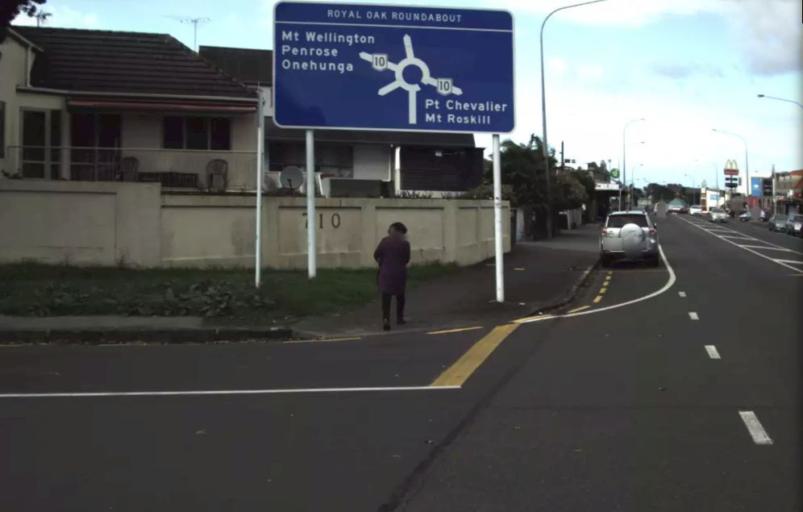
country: NZ
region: Auckland
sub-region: Auckland
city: Auckland
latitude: -36.9093
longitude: 174.7755
